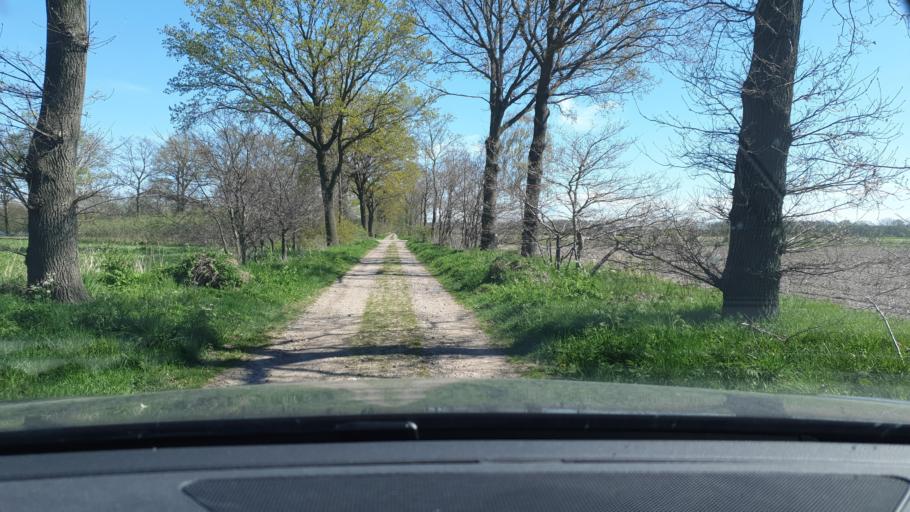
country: NL
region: Limburg
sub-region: Gemeente Venlo
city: Arcen
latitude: 51.4434
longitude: 6.1110
